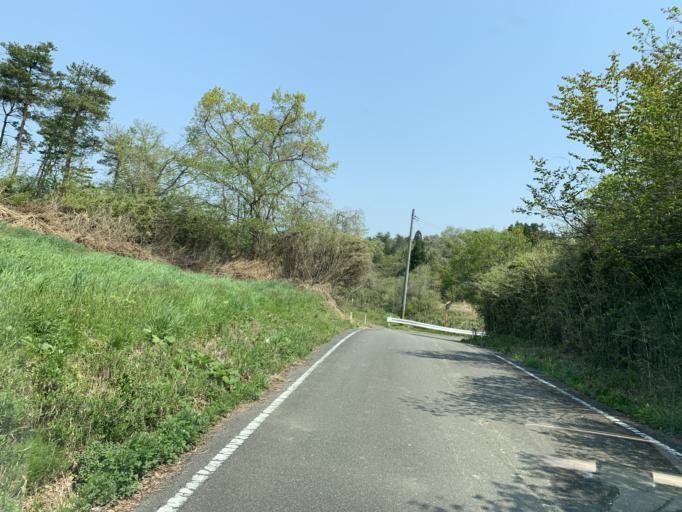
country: JP
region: Iwate
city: Ichinoseki
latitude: 38.8571
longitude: 141.0795
